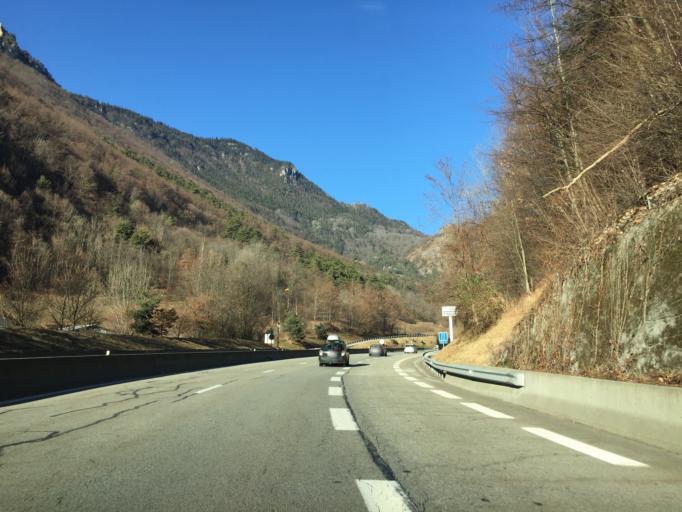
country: FR
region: Rhone-Alpes
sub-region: Departement de la Savoie
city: Moutiers
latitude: 45.5105
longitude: 6.5651
